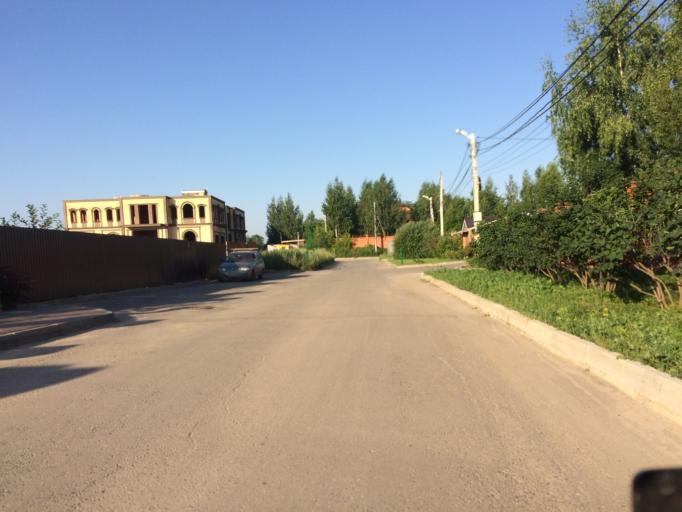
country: RU
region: Mariy-El
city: Yoshkar-Ola
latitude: 56.6471
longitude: 47.9157
